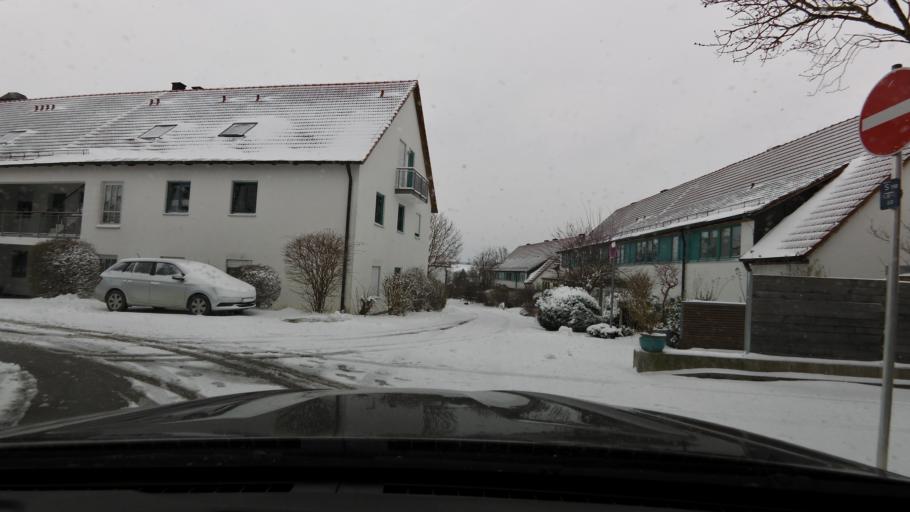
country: DE
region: Bavaria
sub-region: Lower Bavaria
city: Vilsheim
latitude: 48.4503
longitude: 12.1049
